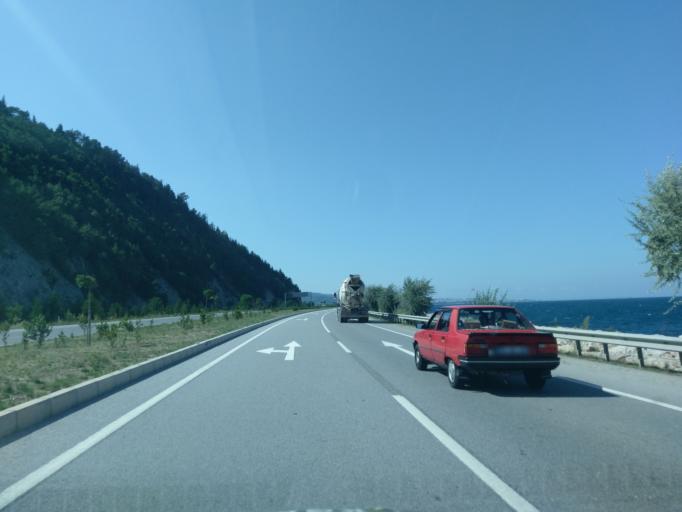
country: TR
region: Sinop
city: Gerze
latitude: 41.7474
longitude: 35.2434
